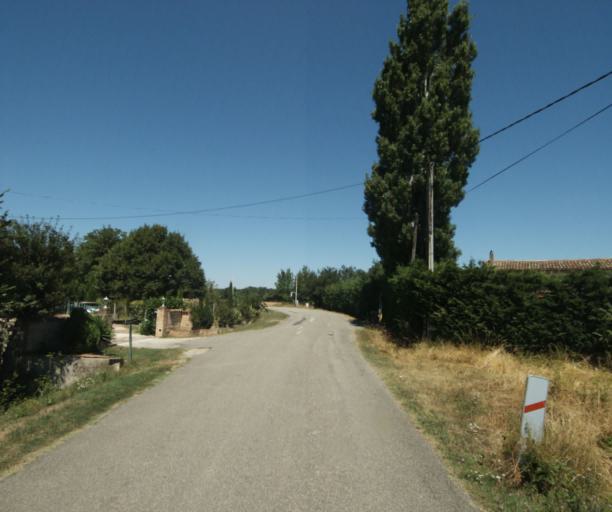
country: FR
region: Midi-Pyrenees
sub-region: Departement de la Haute-Garonne
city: Saint-Felix-Lauragais
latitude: 43.4504
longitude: 1.9375
